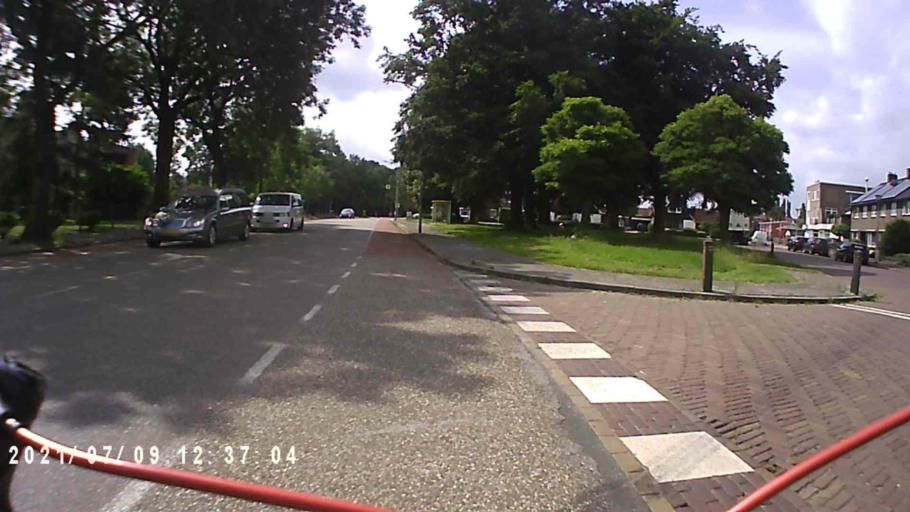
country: NL
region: Groningen
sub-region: Gemeente  Oldambt
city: Winschoten
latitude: 53.1462
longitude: 7.0235
